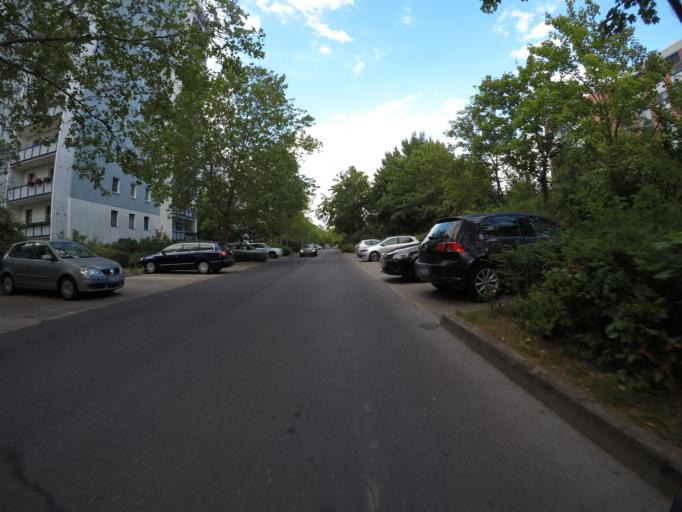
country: DE
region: Berlin
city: Kaulsdorf
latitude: 52.5210
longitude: 13.5930
